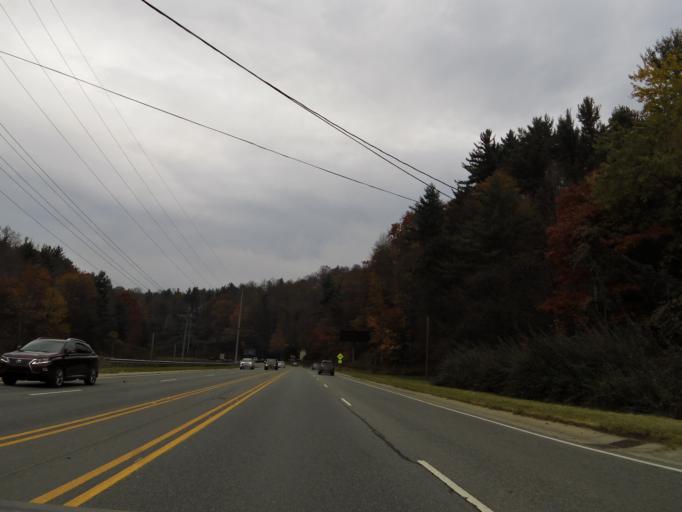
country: US
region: North Carolina
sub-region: Watauga County
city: Boone
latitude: 36.1765
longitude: -81.6481
